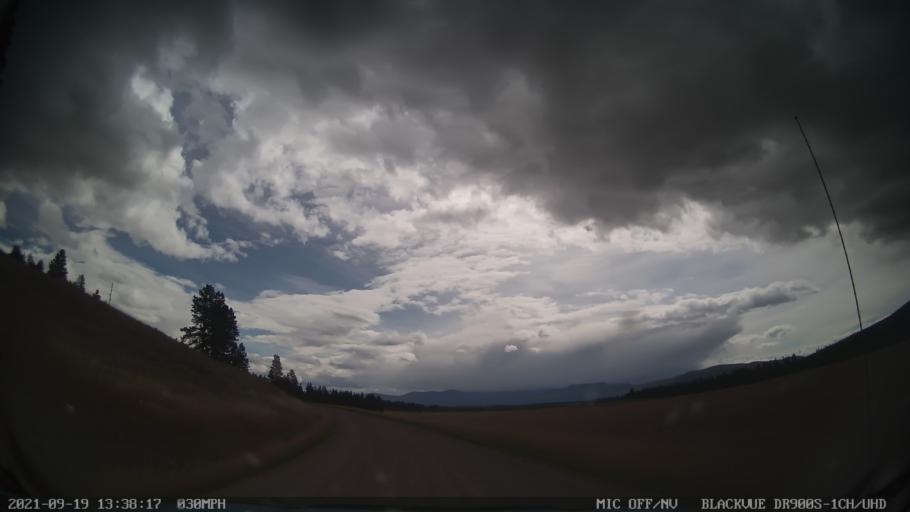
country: US
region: Montana
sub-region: Missoula County
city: Seeley Lake
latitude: 47.1057
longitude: -113.2723
